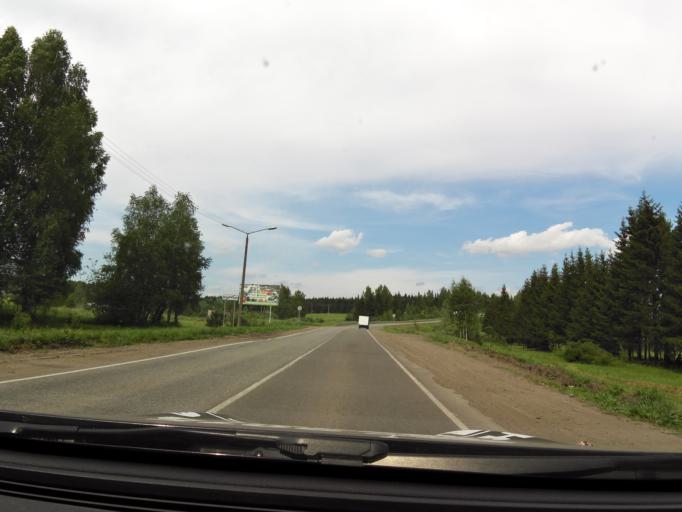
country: RU
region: Kirov
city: Vakhrushi
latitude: 58.6888
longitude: 50.0405
